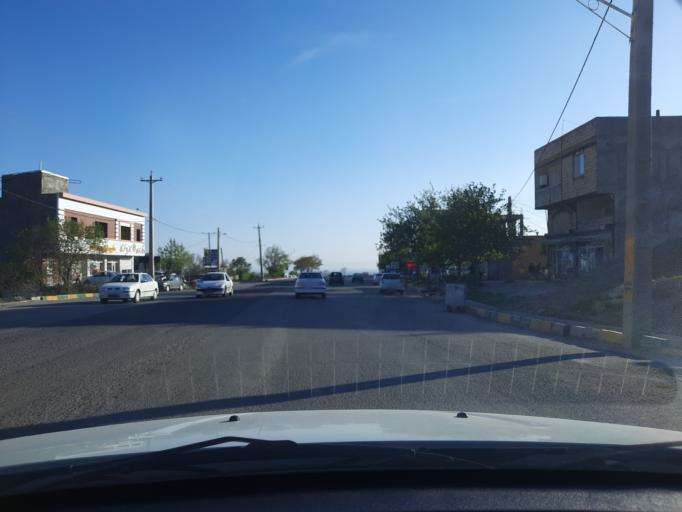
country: IR
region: Qazvin
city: Qazvin
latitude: 36.3312
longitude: 50.1503
